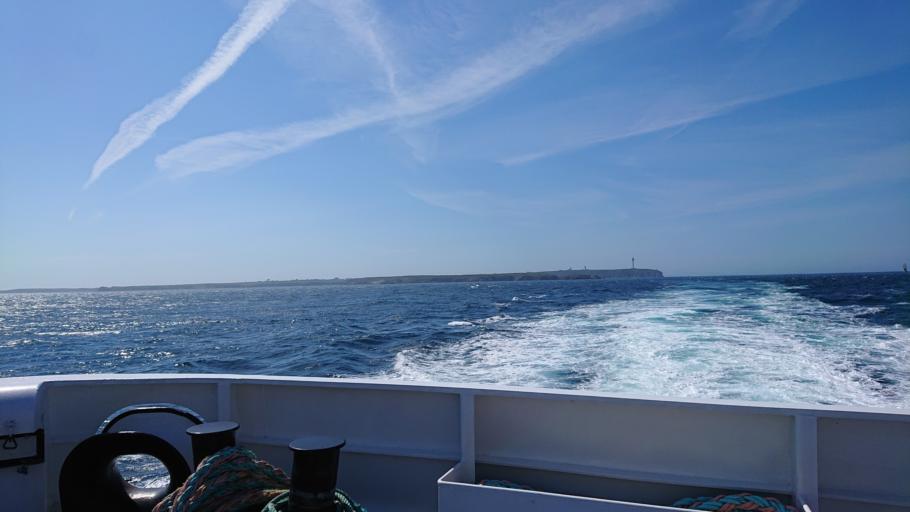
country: FR
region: Brittany
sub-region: Departement du Finistere
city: Porspoder
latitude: 48.4527
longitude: -5.0098
